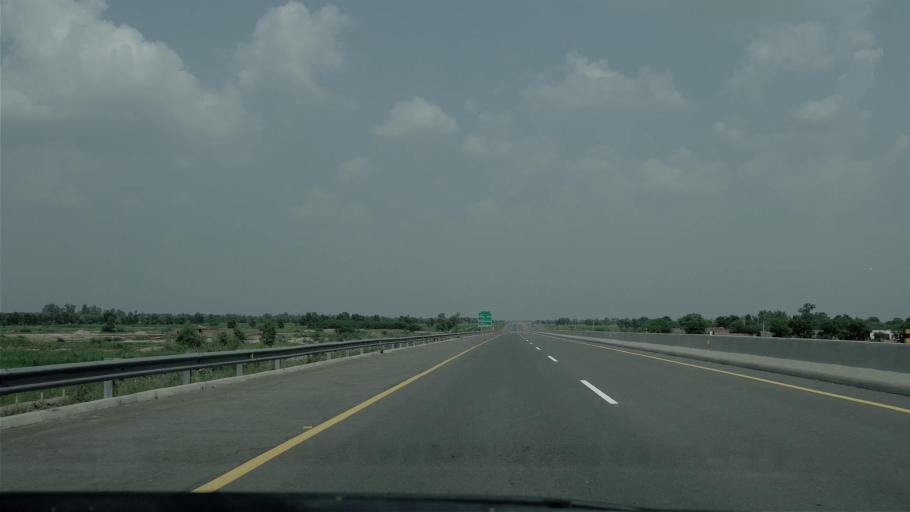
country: PK
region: Punjab
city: Gojra
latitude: 31.1958
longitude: 72.6544
